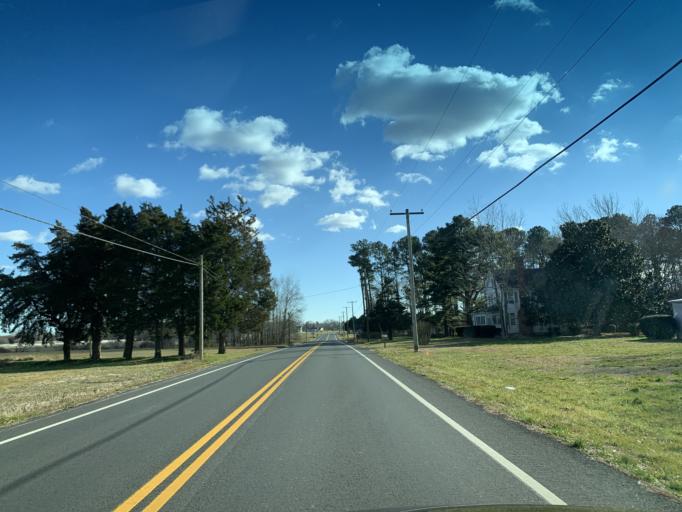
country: US
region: Maryland
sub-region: Worcester County
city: Berlin
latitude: 38.3541
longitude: -75.1955
